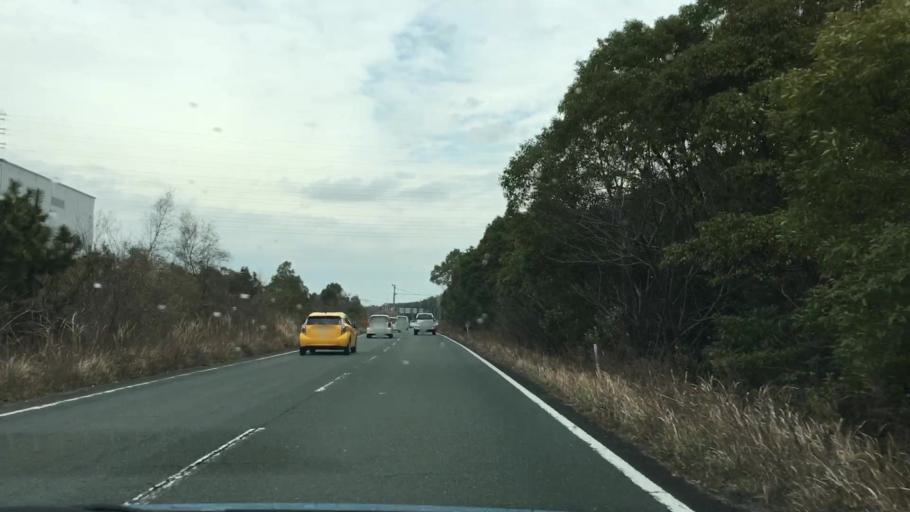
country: JP
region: Aichi
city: Toyohashi
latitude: 34.7112
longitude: 137.3357
